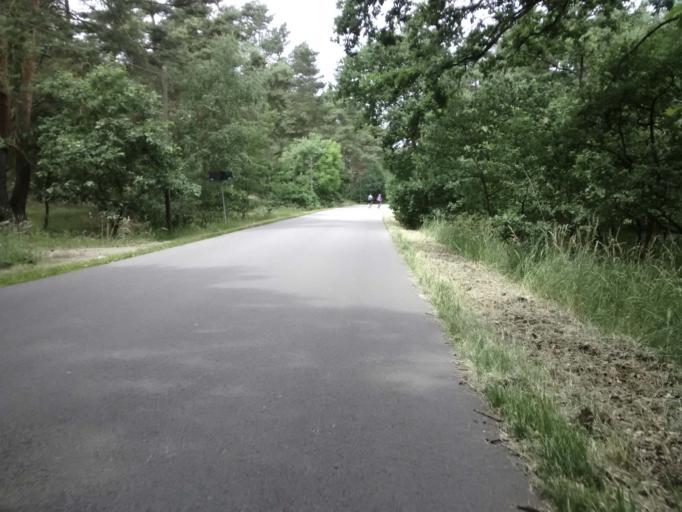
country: DE
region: Brandenburg
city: Ruhstadt
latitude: 52.9536
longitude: 11.8508
